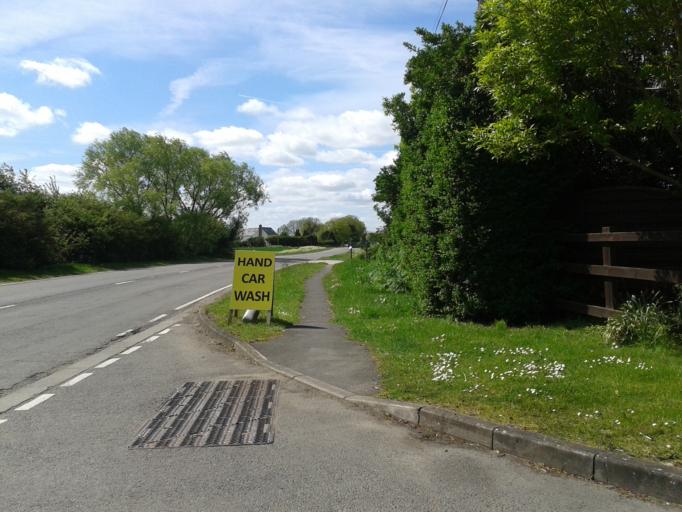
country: GB
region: England
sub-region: Cambridgeshire
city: Melbourn
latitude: 52.0982
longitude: 0.0361
